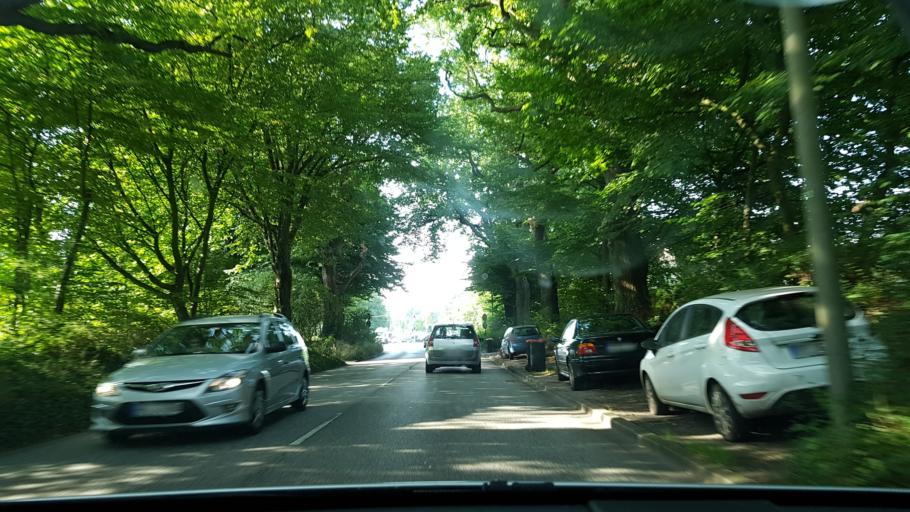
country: DE
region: Hamburg
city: Farmsen-Berne
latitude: 53.6305
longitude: 10.1418
